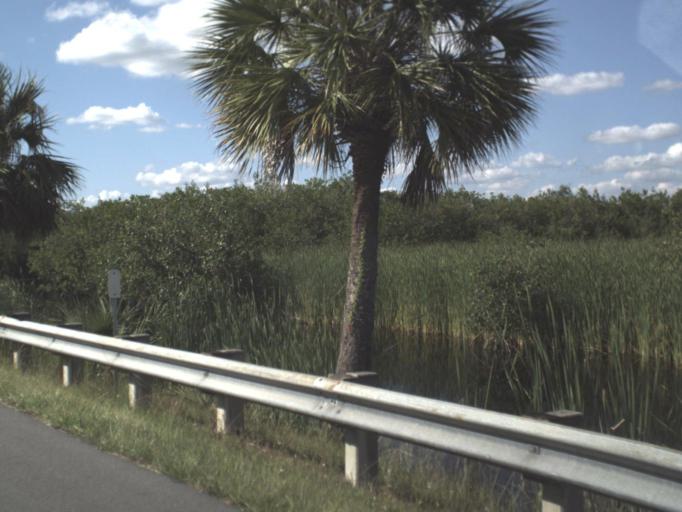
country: US
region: Florida
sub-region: Collier County
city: Marco
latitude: 25.9100
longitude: -81.3624
